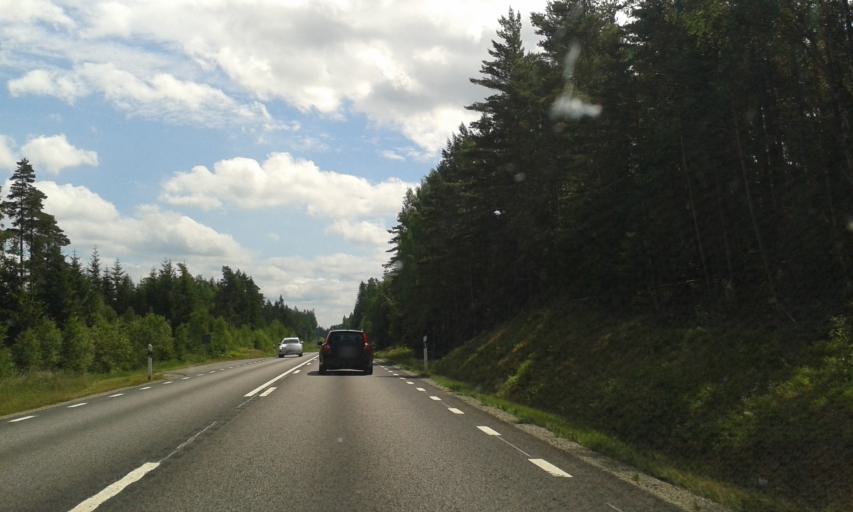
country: SE
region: Joenkoeping
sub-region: Varnamo Kommun
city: Bor
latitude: 57.0608
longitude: 14.1938
